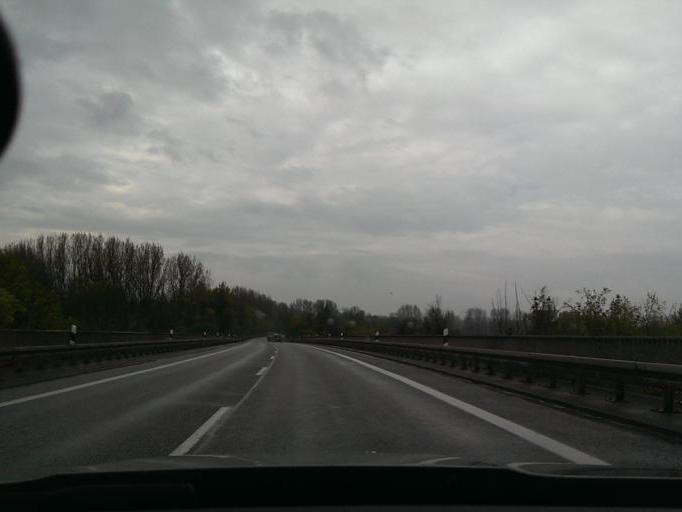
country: DE
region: Lower Saxony
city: Laatzen
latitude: 52.2889
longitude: 9.8163
